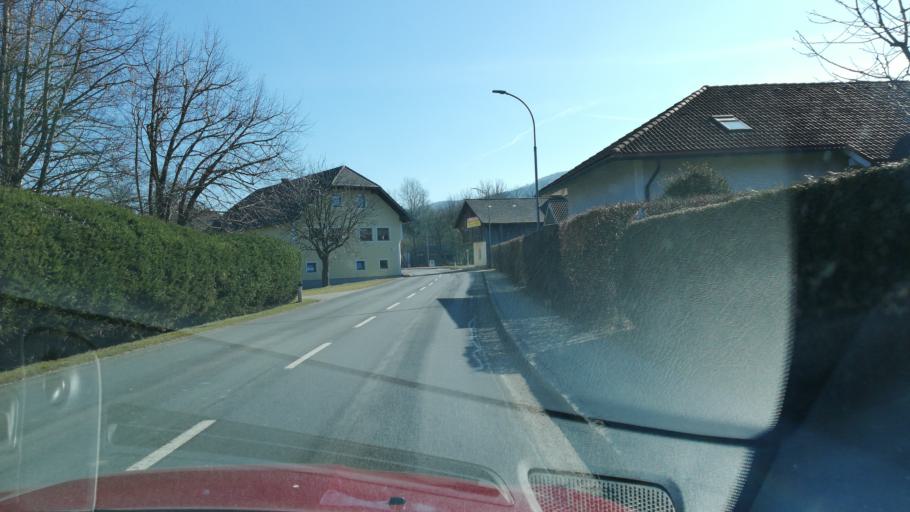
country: AT
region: Upper Austria
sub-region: Politischer Bezirk Vocklabruck
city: Aurach am Hongar
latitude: 47.9518
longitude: 13.6689
